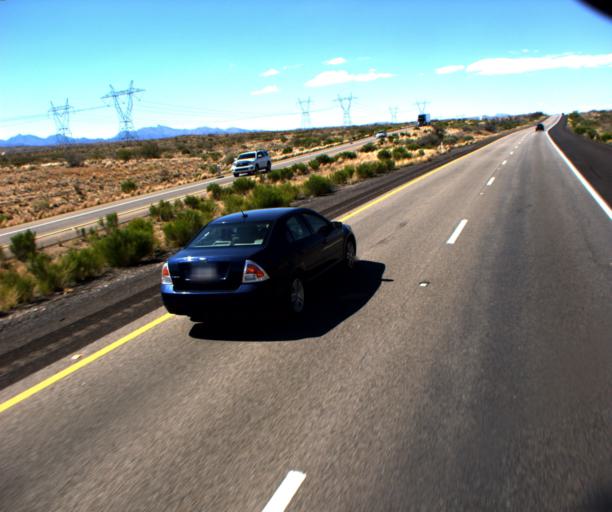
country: US
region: Arizona
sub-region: Mohave County
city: Kingman
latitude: 34.9494
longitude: -113.6677
